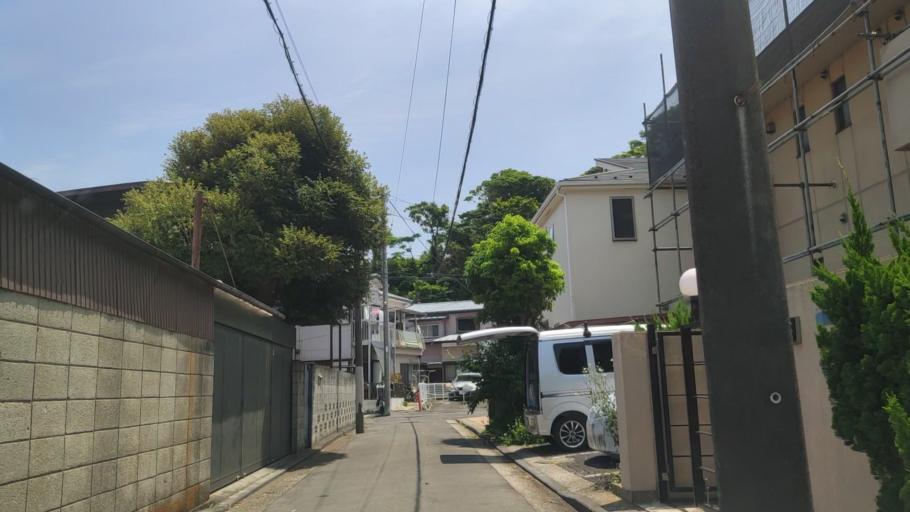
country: JP
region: Kanagawa
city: Yokohama
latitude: 35.4177
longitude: 139.6650
